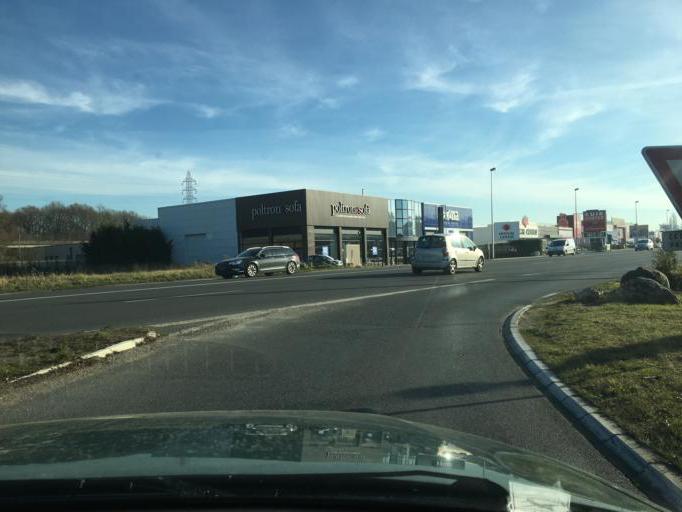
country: FR
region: Centre
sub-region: Departement du Loiret
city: Saran
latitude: 47.9608
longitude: 1.8892
